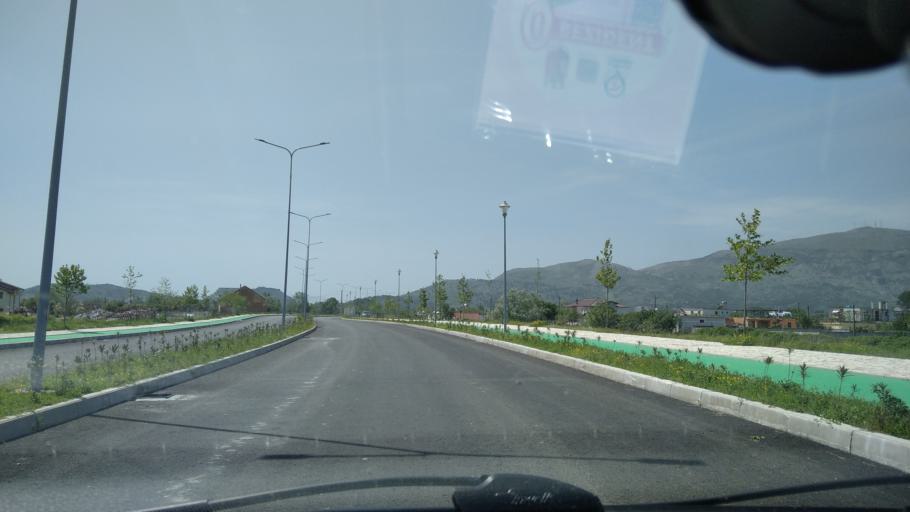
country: AL
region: Shkoder
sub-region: Rrethi i Shkodres
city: Shkoder
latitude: 42.0807
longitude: 19.4924
